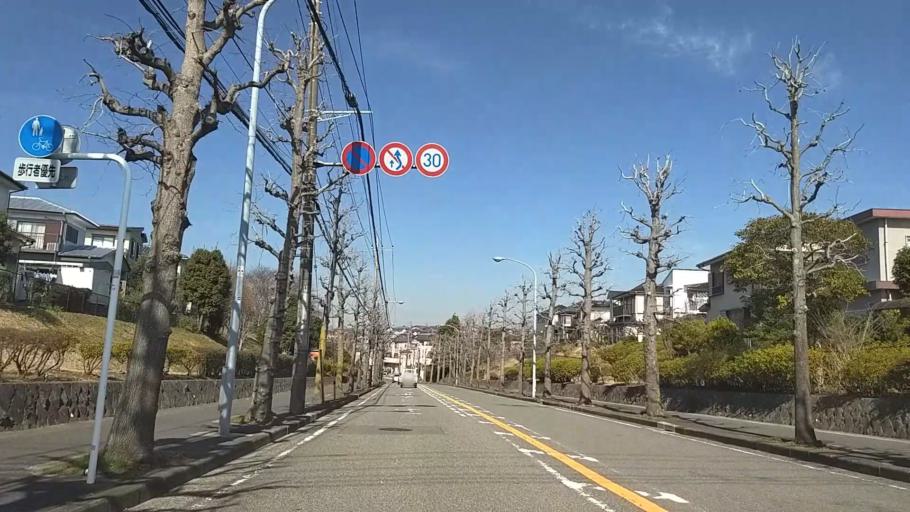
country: JP
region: Kanagawa
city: Kamakura
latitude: 35.3730
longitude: 139.5454
